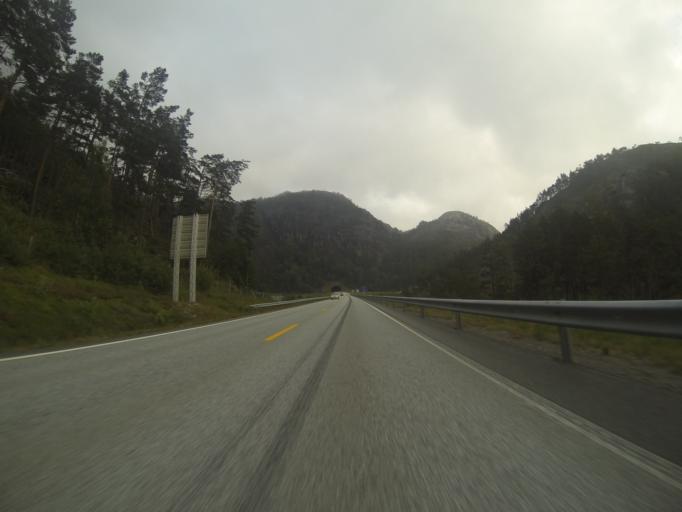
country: NO
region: Hordaland
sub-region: Odda
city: Odda
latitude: 59.8804
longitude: 6.4371
